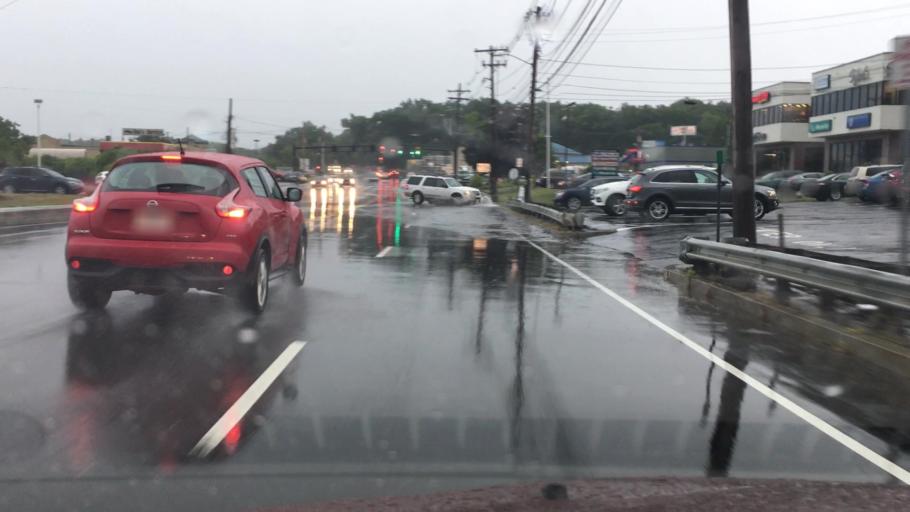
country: US
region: Massachusetts
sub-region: Middlesex County
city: Lexington
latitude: 42.4735
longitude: -71.2127
